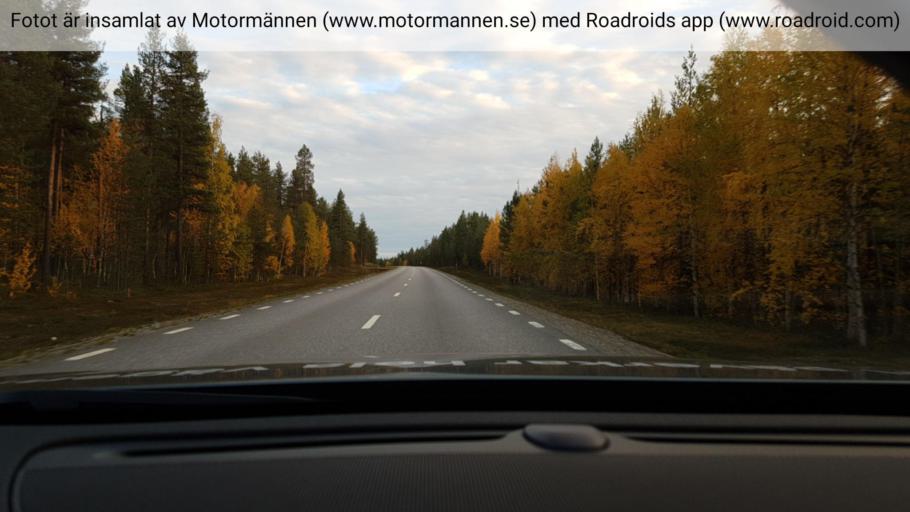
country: SE
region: Norrbotten
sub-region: Jokkmokks Kommun
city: Jokkmokk
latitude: 66.3997
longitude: 19.6945
